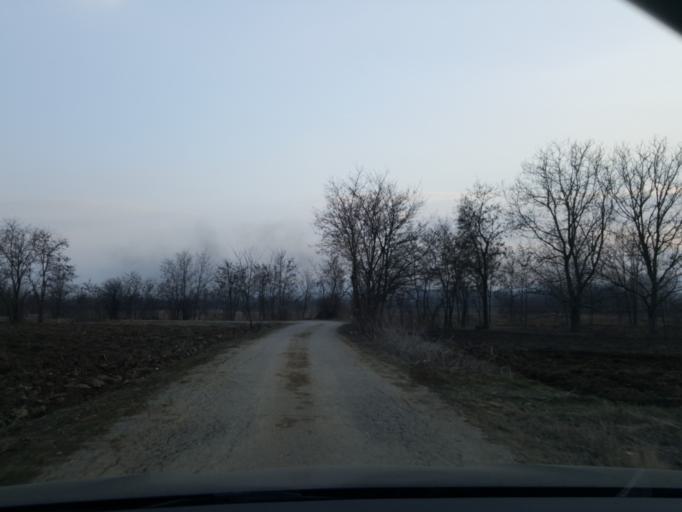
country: RS
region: Central Serbia
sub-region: Nisavski Okrug
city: Aleksinac
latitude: 43.5704
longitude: 21.6415
